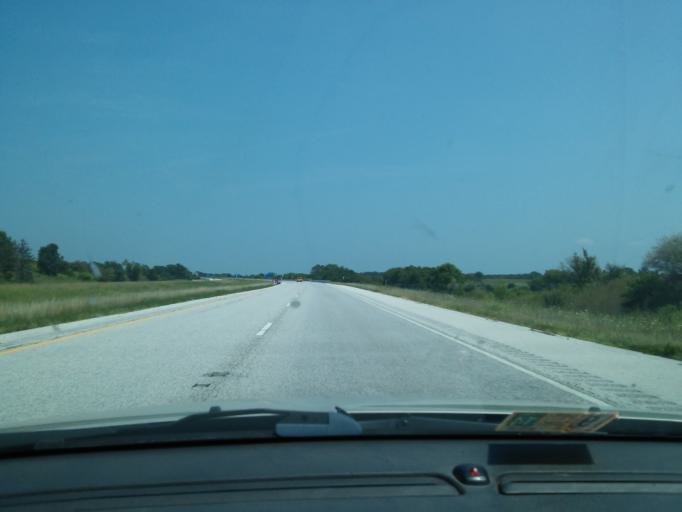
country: US
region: Illinois
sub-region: Morgan County
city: South Jacksonville
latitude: 39.6803
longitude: -90.2708
